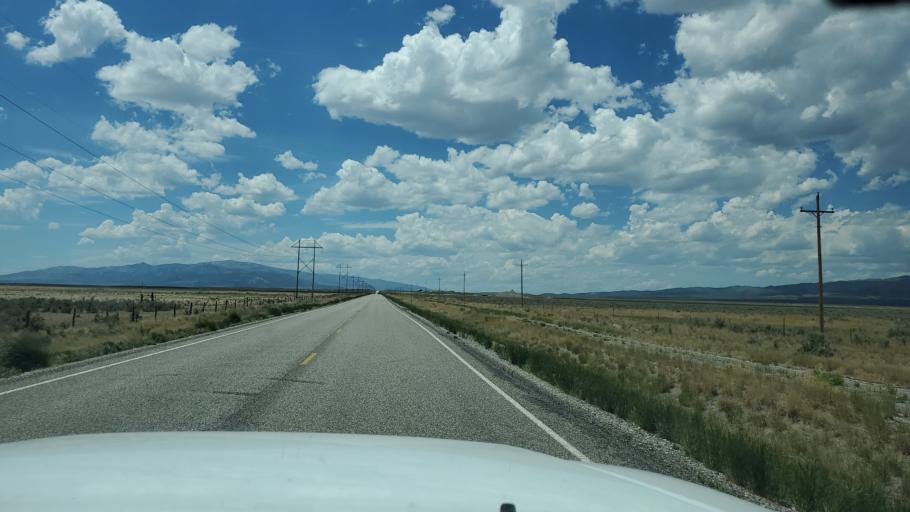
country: US
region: Idaho
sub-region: Oneida County
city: Malad City
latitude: 41.9662
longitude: -112.9696
